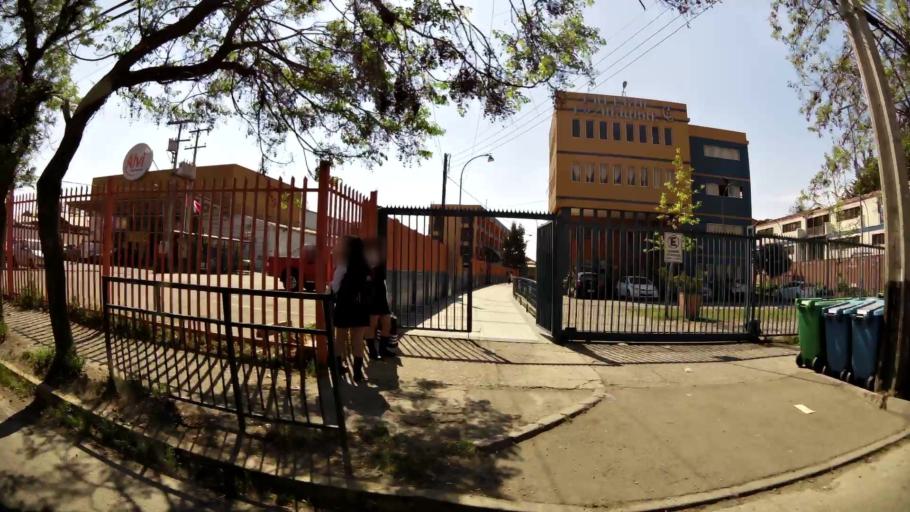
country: CL
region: Santiago Metropolitan
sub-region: Provincia de Cordillera
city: Puente Alto
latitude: -33.6163
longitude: -70.6093
